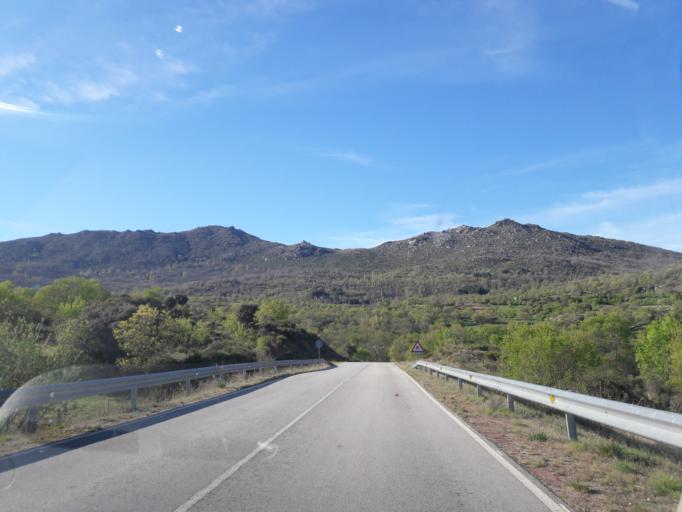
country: ES
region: Castille and Leon
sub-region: Provincia de Salamanca
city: Sanchotello
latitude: 40.4457
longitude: -5.7361
